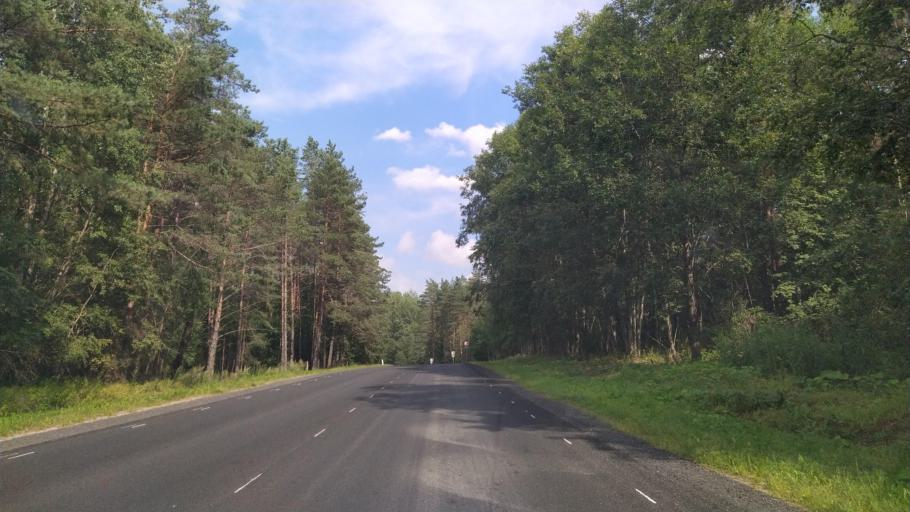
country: RU
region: Pskov
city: Porkhov
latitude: 57.7339
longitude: 29.4034
